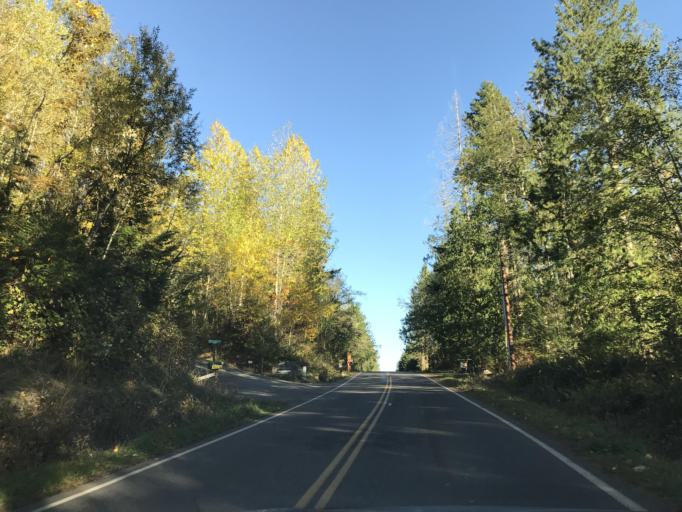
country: US
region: Washington
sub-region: Whatcom County
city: Geneva
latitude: 48.7678
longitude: -122.3848
